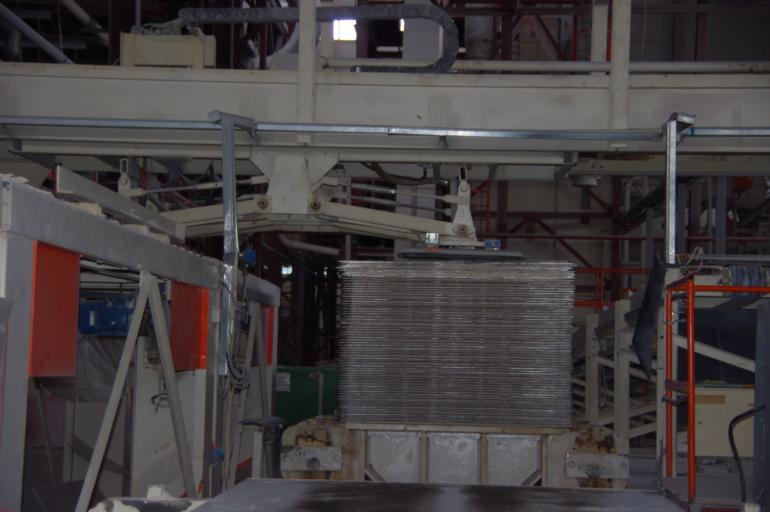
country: RU
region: Nizjnij Novgorod
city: Arzamas
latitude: 55.2989
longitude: 43.9291
